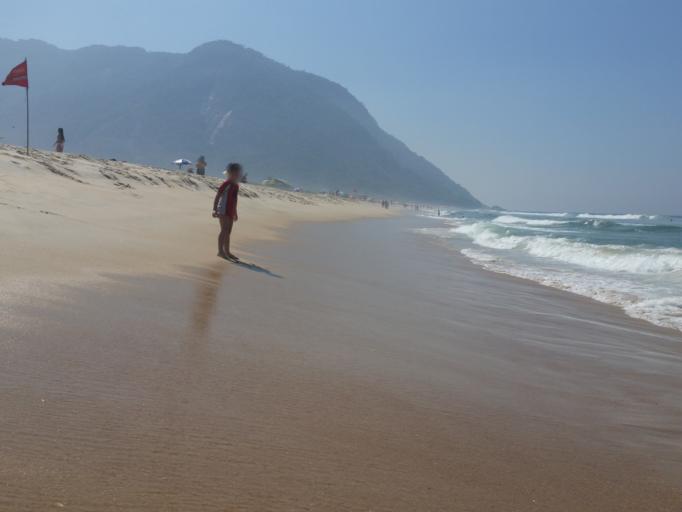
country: BR
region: Rio de Janeiro
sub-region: Nilopolis
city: Nilopolis
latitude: -23.0493
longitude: -43.5282
